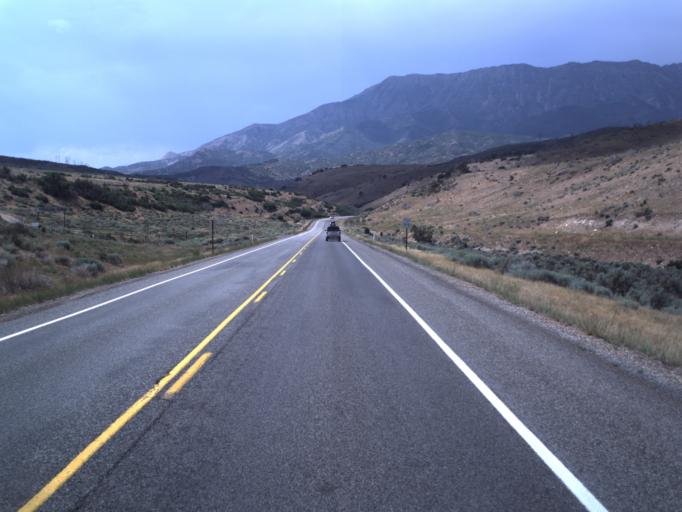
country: US
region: Utah
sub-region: Sanpete County
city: Fountain Green
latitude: 39.6956
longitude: -111.6925
